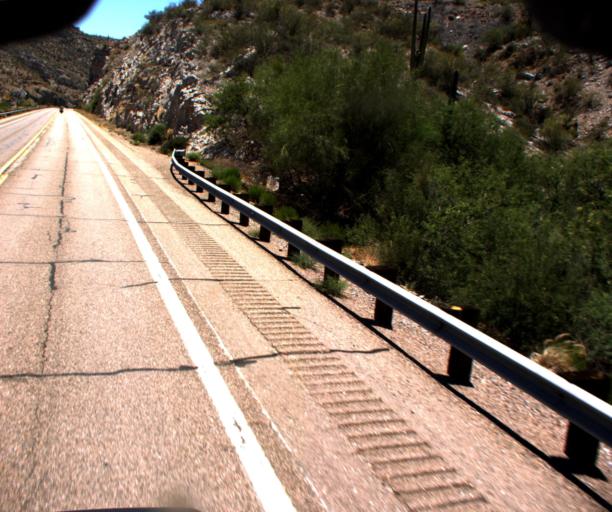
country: US
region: Arizona
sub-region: Pinal County
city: Kearny
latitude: 33.0105
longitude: -110.7519
